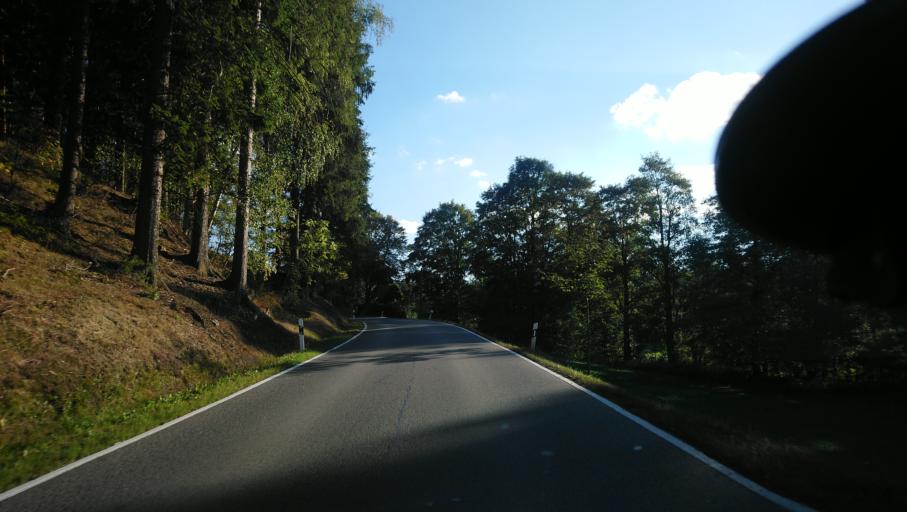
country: DE
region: Saxony
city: Crottendorf
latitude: 50.5372
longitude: 12.9464
